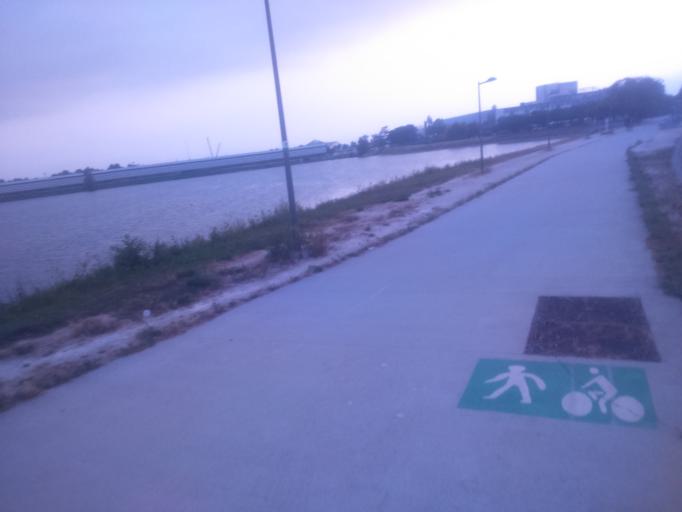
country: FR
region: Aquitaine
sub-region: Departement de la Gironde
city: Le Bouscat
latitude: 44.8884
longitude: -0.5685
